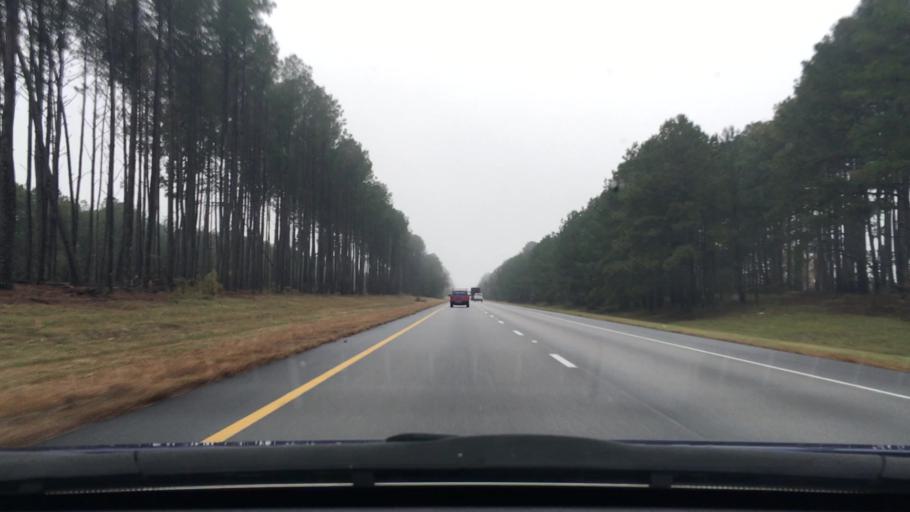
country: US
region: South Carolina
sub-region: Lee County
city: Bishopville
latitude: 34.2027
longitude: -80.3622
